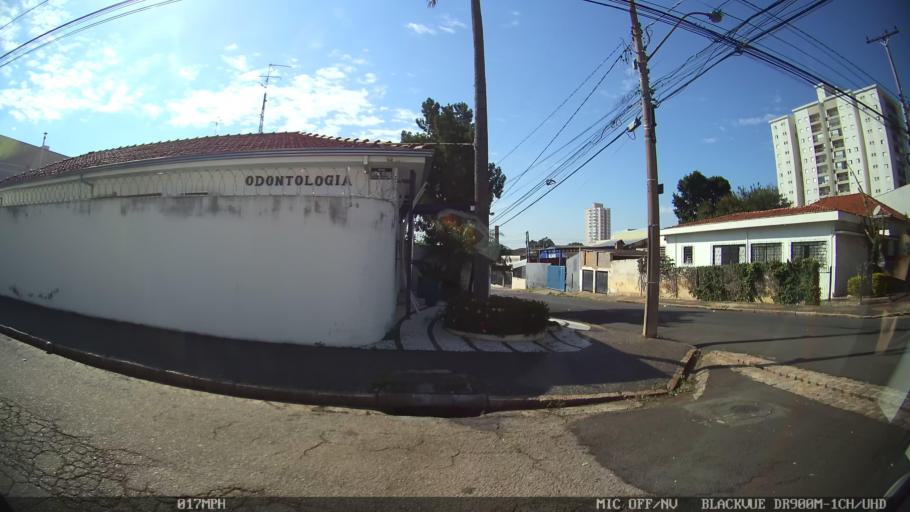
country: BR
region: Sao Paulo
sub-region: Americana
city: Americana
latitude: -22.7455
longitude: -47.3276
